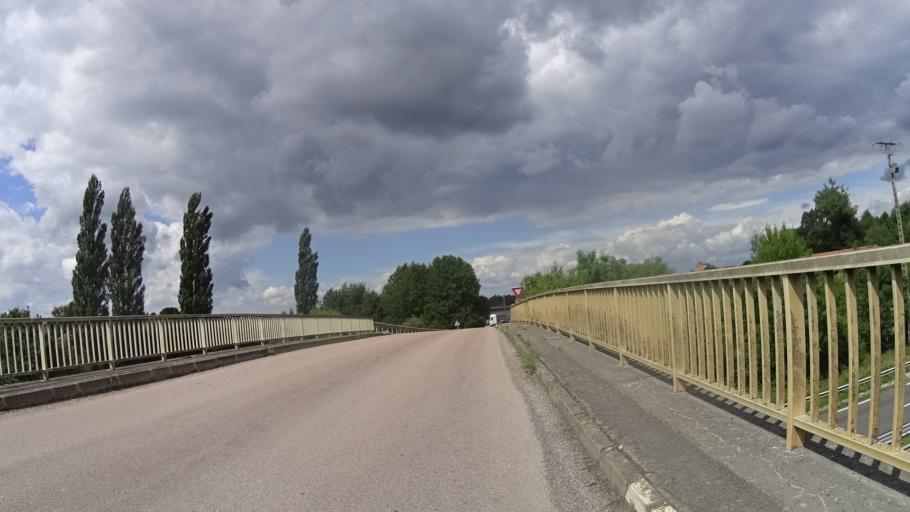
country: FR
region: Champagne-Ardenne
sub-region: Departement de la Haute-Marne
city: Villiers-en-Lieu
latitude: 48.6529
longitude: 4.8279
